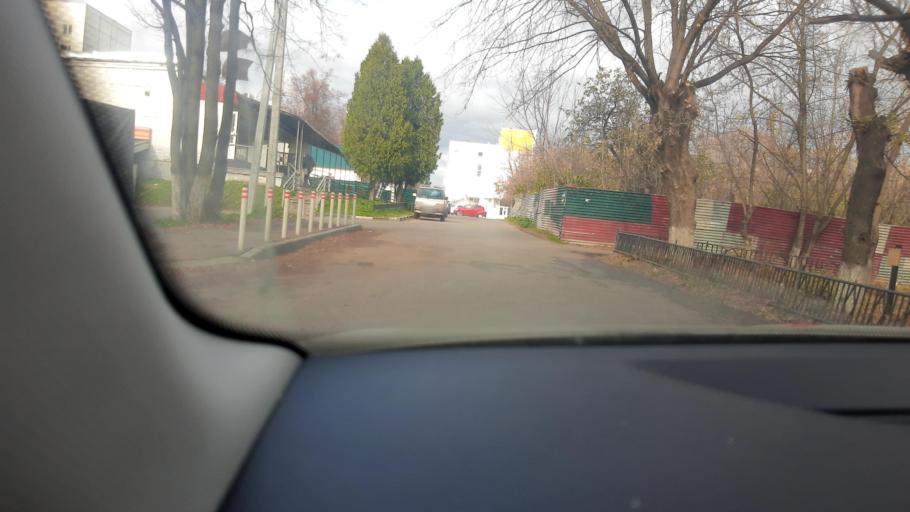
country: RU
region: Moskovskaya
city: Shcherbinka
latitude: 55.4713
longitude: 37.6134
